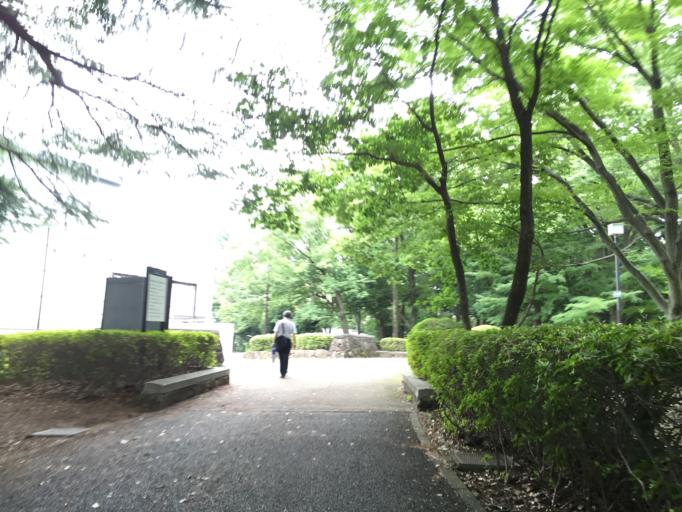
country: JP
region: Tokyo
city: Kokubunji
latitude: 35.6742
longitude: 139.4927
